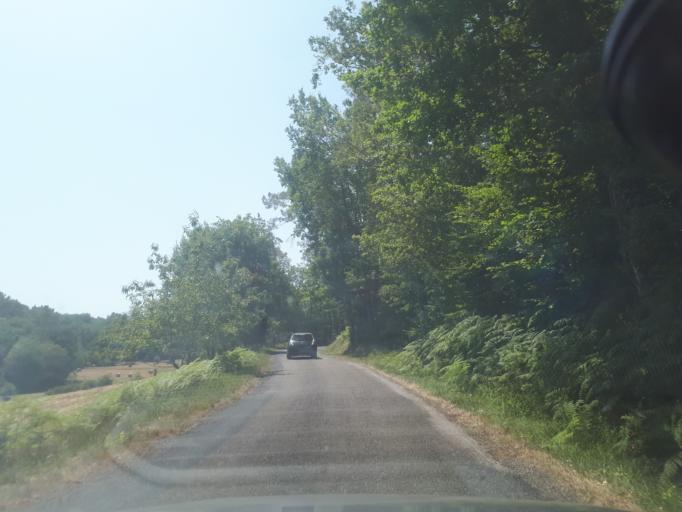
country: FR
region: Midi-Pyrenees
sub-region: Departement du Lot
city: Gourdon
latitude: 44.7478
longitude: 1.3345
